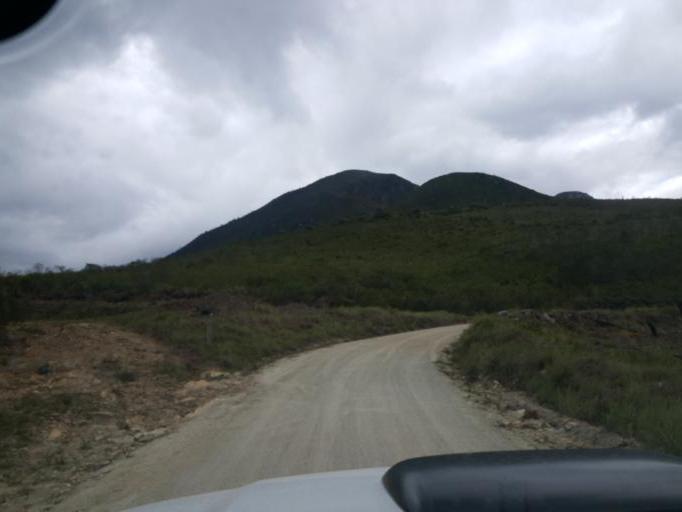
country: ZA
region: Western Cape
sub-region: Eden District Municipality
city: George
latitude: -33.9199
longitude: 22.4155
